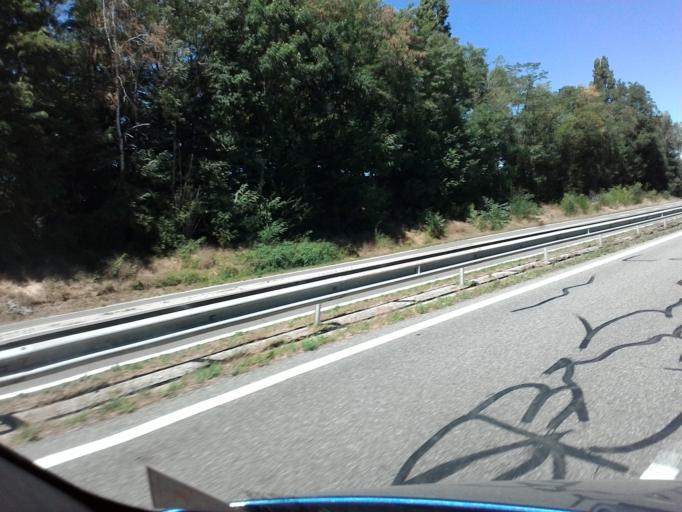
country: FR
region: Bourgogne
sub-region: Departement de Saone-et-Loire
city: Cuiseaux
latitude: 46.5031
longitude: 5.3857
